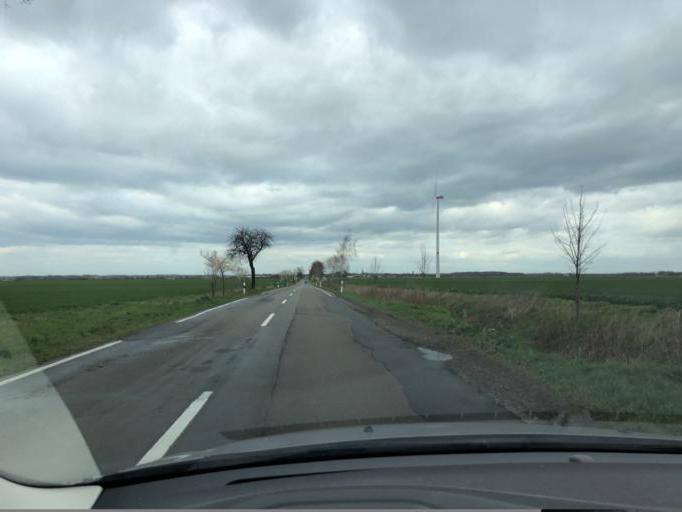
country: DE
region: Saxony-Anhalt
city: Lutzen
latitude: 51.2266
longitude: 12.1396
